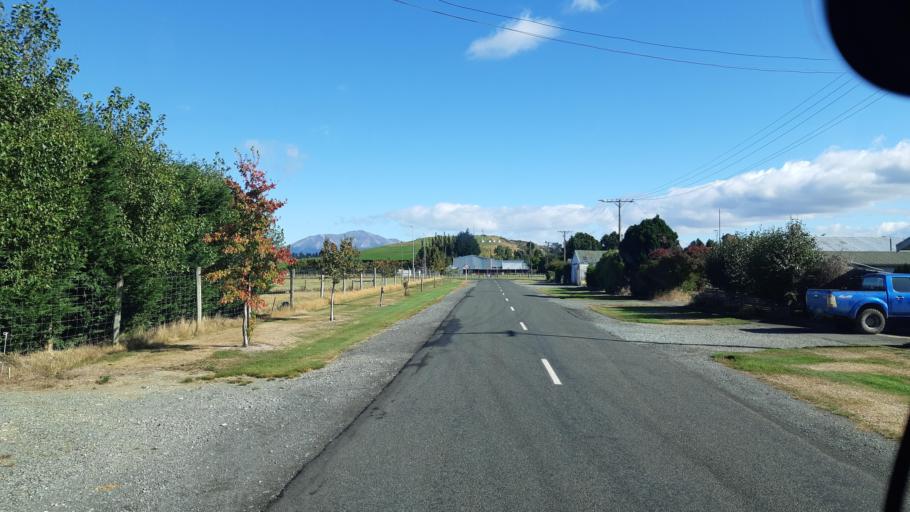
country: NZ
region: Southland
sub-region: Southland District
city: Winton
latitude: -45.6705
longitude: 168.2376
